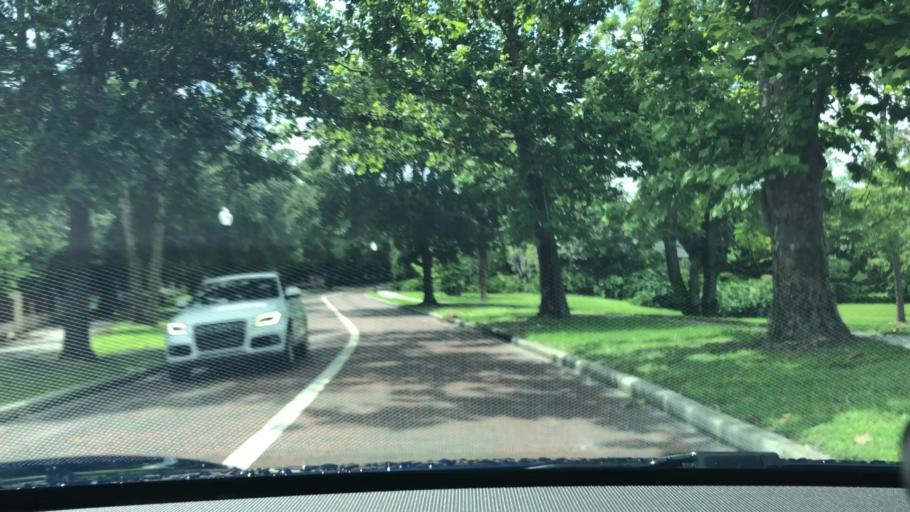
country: US
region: Florida
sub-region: Orange County
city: Winter Park
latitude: 28.5829
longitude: -81.3528
